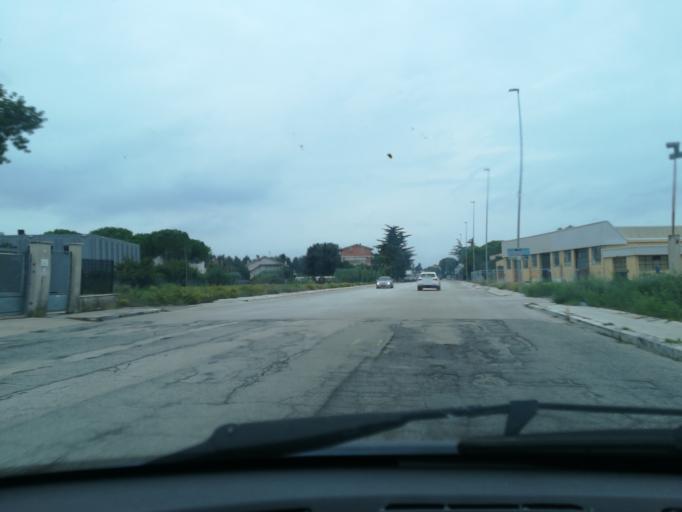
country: IT
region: The Marches
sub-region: Provincia di Macerata
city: Piediripa
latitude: 43.2767
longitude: 13.4987
